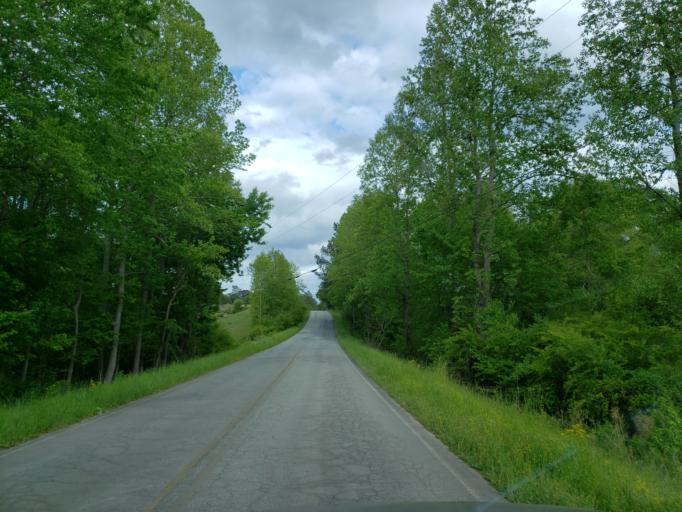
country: US
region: Georgia
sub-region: Haralson County
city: Tallapoosa
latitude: 33.7853
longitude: -85.3344
